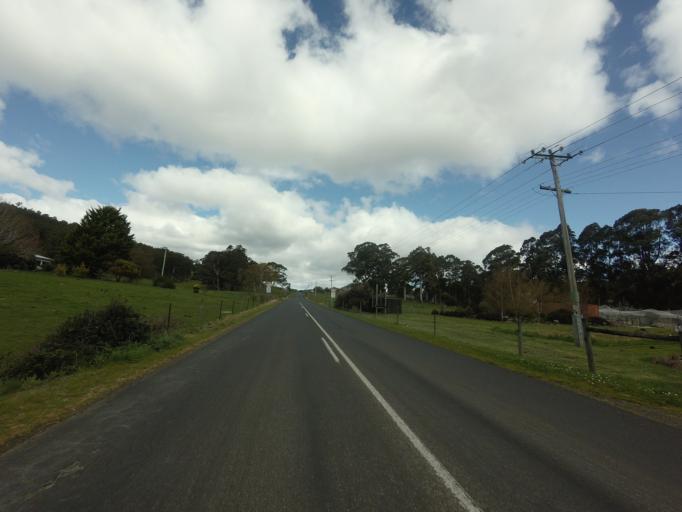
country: AU
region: Tasmania
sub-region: Huon Valley
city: Geeveston
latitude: -43.1790
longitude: 146.9256
